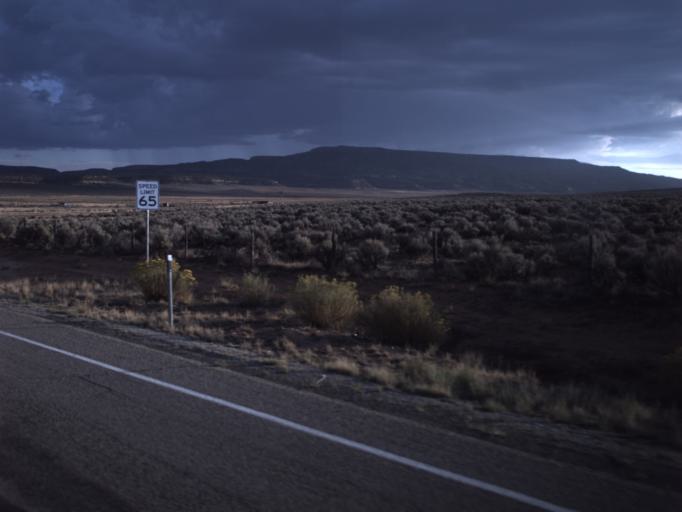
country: US
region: Utah
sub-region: San Juan County
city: Monticello
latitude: 38.0717
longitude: -109.3493
